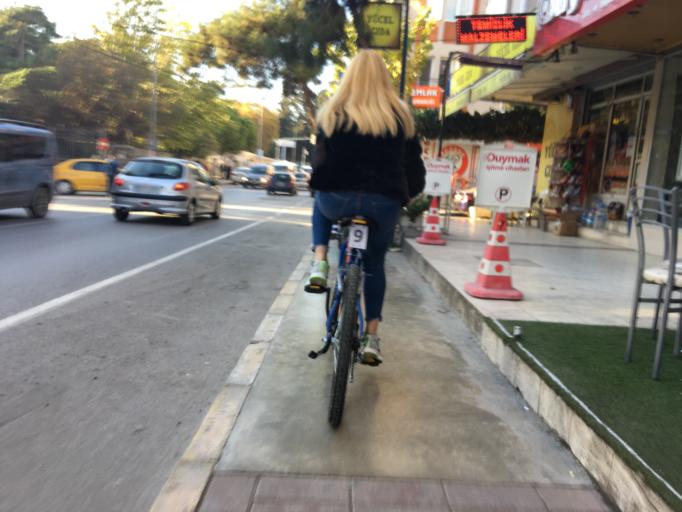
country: TR
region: Izmir
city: Buca
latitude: 38.3846
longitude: 27.1673
